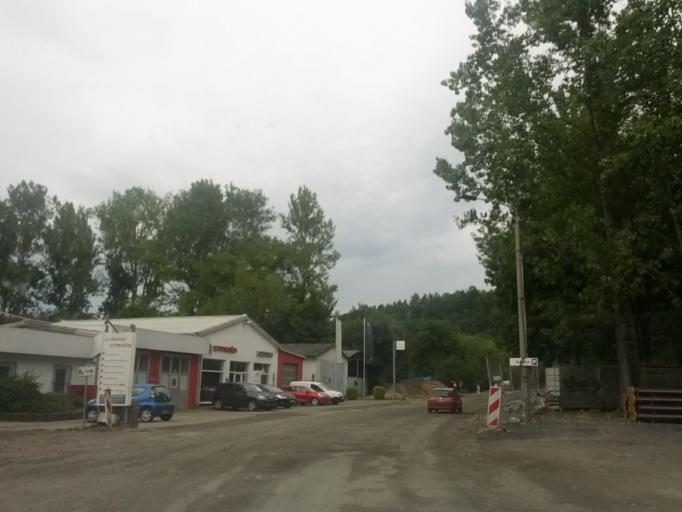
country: DE
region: Thuringia
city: Bad Salzungen
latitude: 50.8163
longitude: 10.2248
